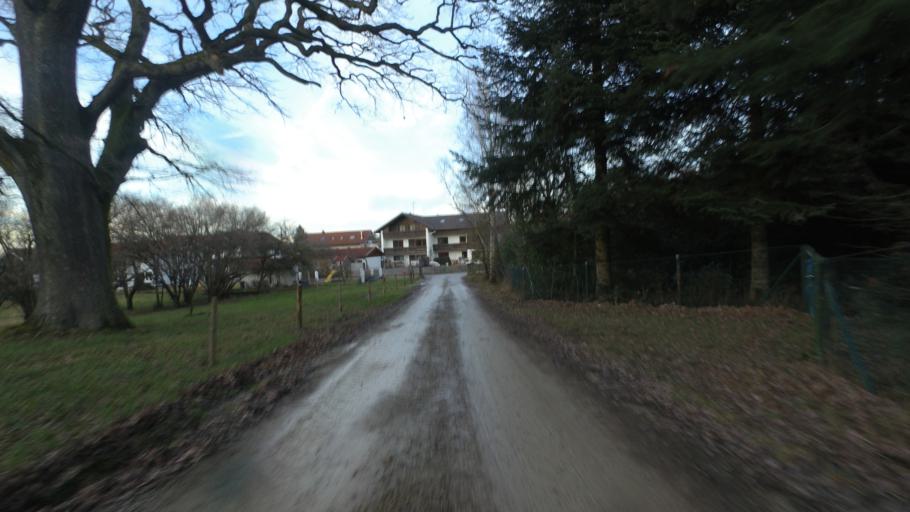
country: DE
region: Bavaria
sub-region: Upper Bavaria
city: Chieming
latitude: 47.8886
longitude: 12.5441
